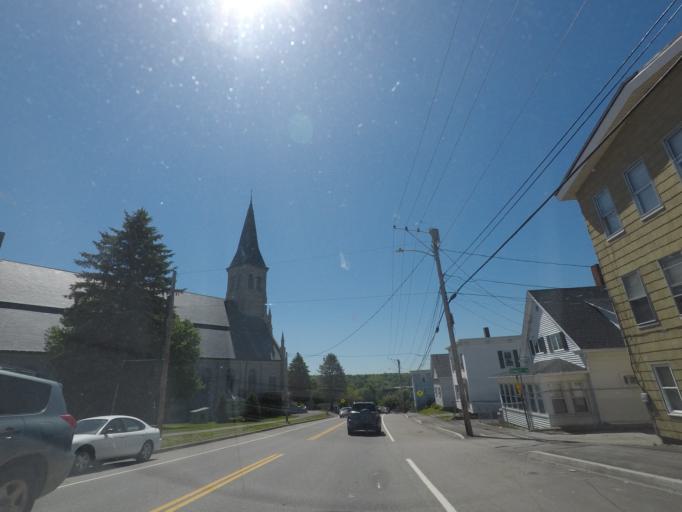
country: US
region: Maine
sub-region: Kennebec County
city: Augusta
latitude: 44.3245
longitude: -69.7744
